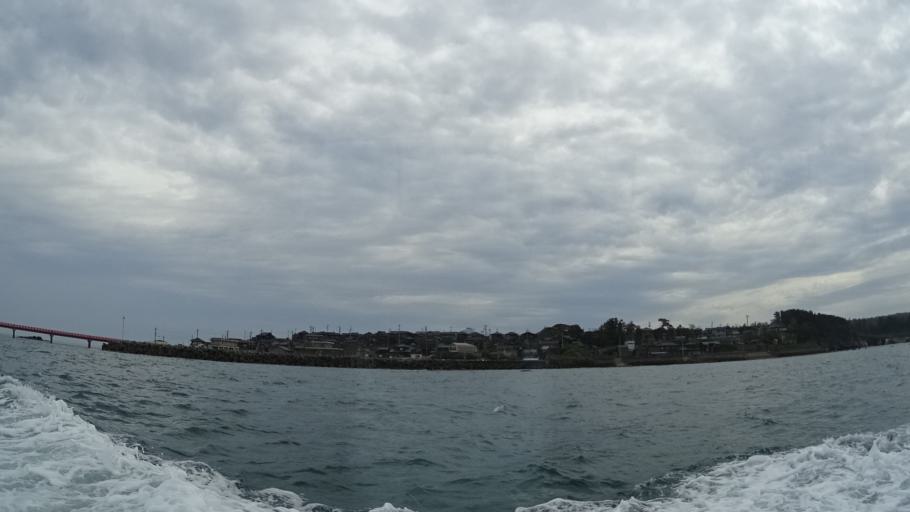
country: JP
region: Fukui
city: Mikuni
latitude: 36.2479
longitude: 136.1210
